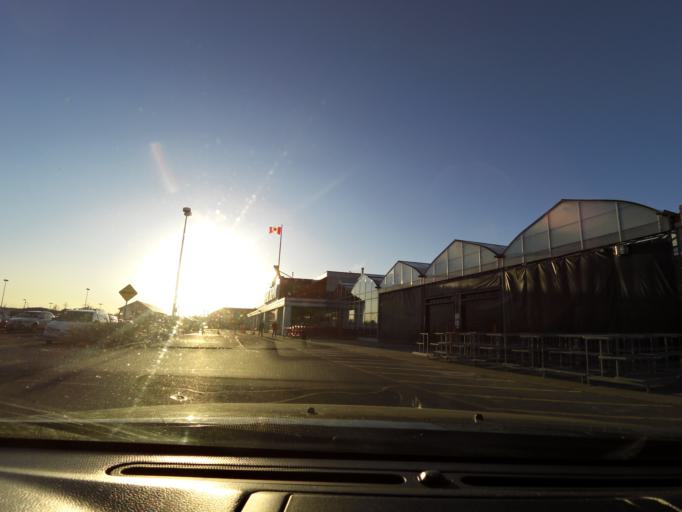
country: CA
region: Ontario
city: Ancaster
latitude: 43.2302
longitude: -79.9435
